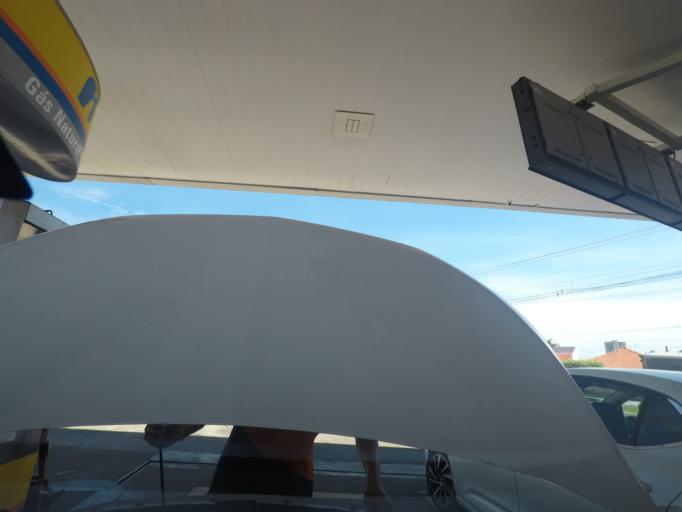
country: BR
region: Sao Paulo
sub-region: Matao
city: Matao
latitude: -21.6153
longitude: -48.3662
